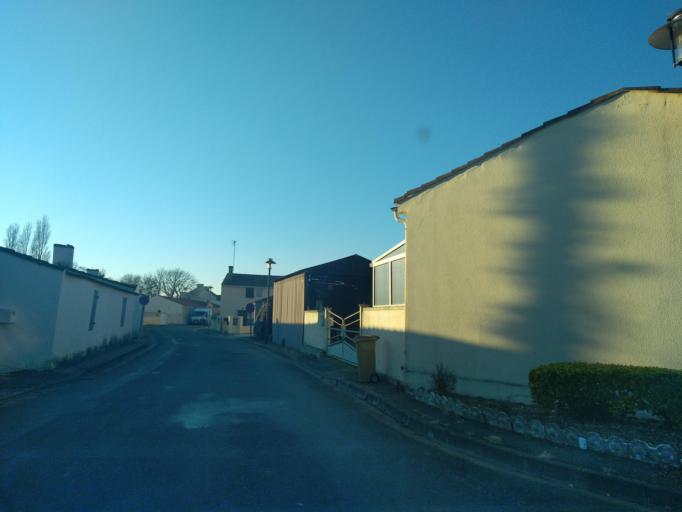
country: FR
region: Pays de la Loire
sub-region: Departement de la Vendee
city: Angles
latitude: 46.3972
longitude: -1.3016
